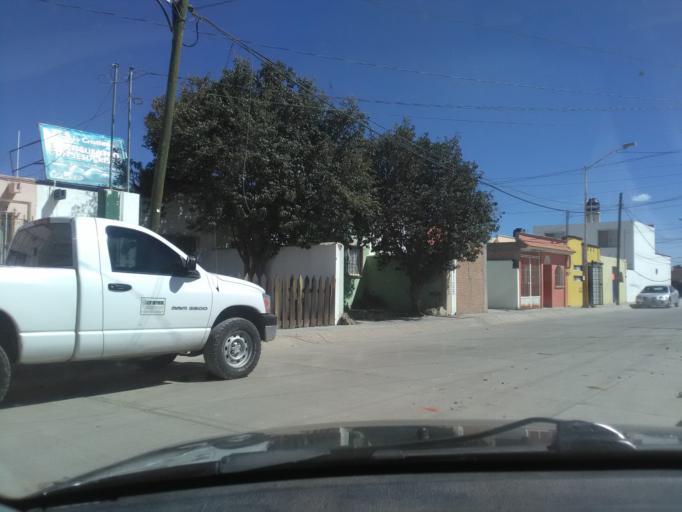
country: MX
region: Durango
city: Victoria de Durango
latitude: 24.0060
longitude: -104.6288
